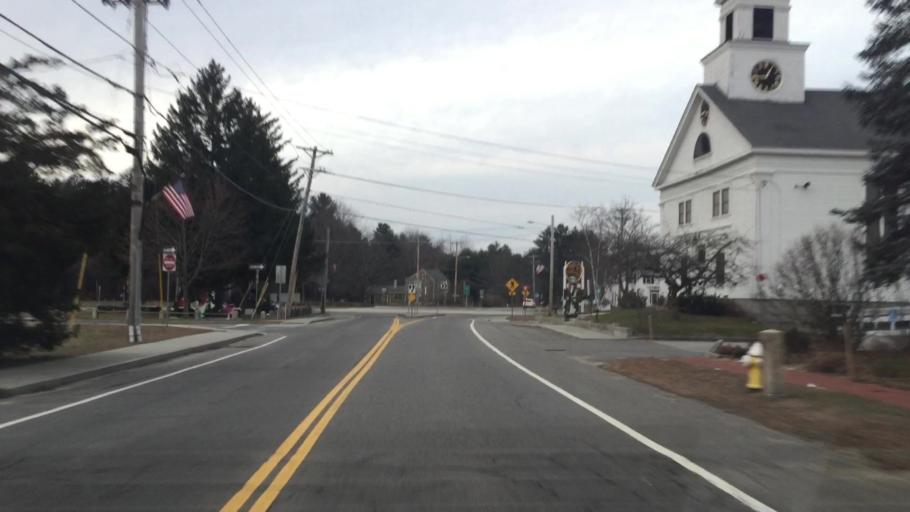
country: US
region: New Hampshire
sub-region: Hillsborough County
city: Pelham
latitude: 42.7337
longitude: -71.3220
